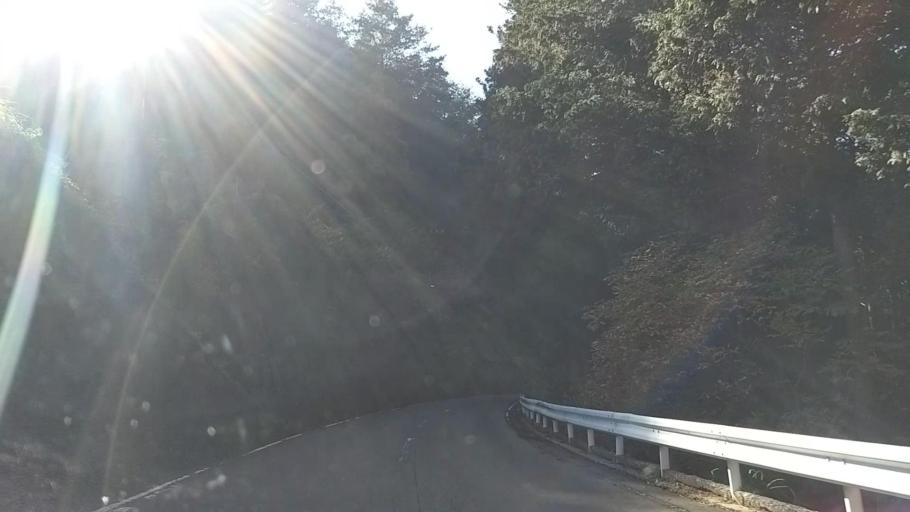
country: JP
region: Yamanashi
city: Otsuki
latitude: 35.7473
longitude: 138.9627
